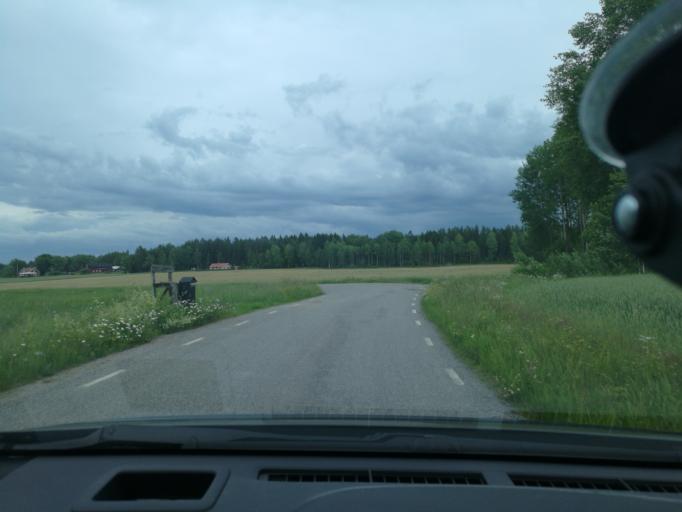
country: SE
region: Vaestmanland
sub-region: Vasteras
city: Skultuna
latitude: 59.8659
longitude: 16.3415
